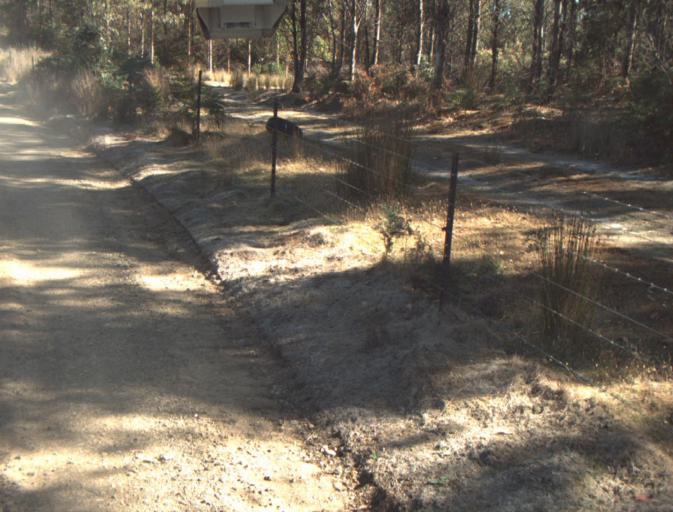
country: AU
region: Tasmania
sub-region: Dorset
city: Scottsdale
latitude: -41.3027
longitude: 147.3586
